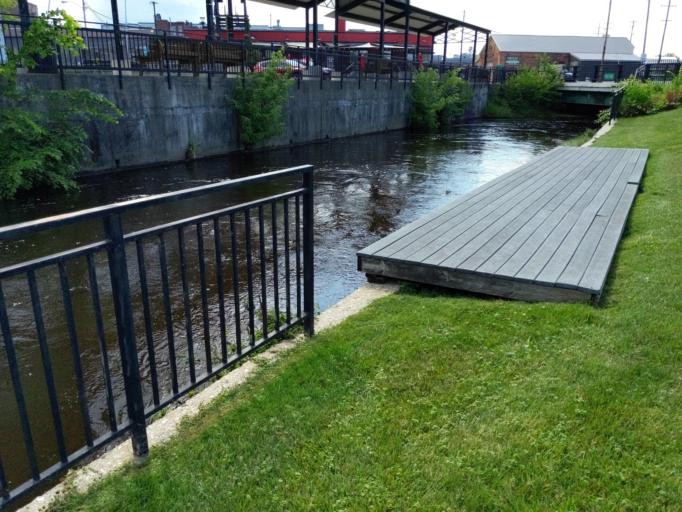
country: US
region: Michigan
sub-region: Jackson County
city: Jackson
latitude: 42.2491
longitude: -84.4063
